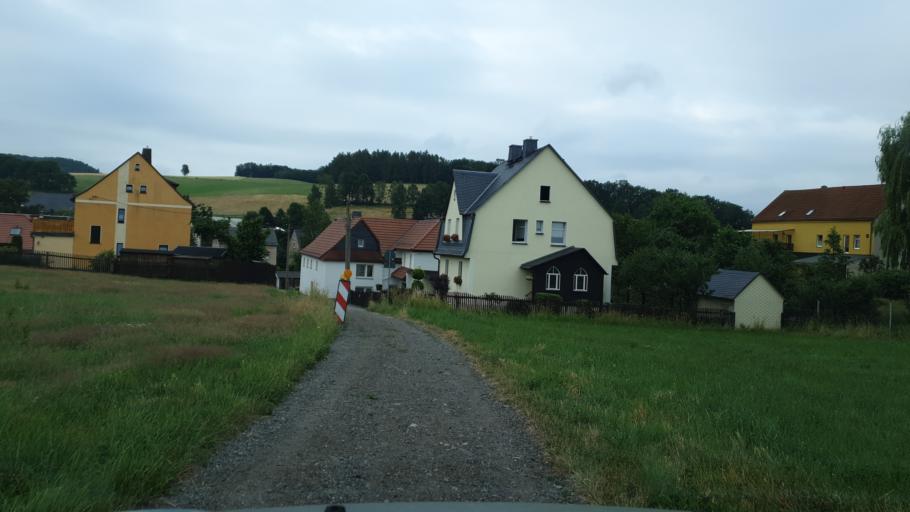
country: DE
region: Saxony
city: Bernsdorf
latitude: 50.7468
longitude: 12.6623
